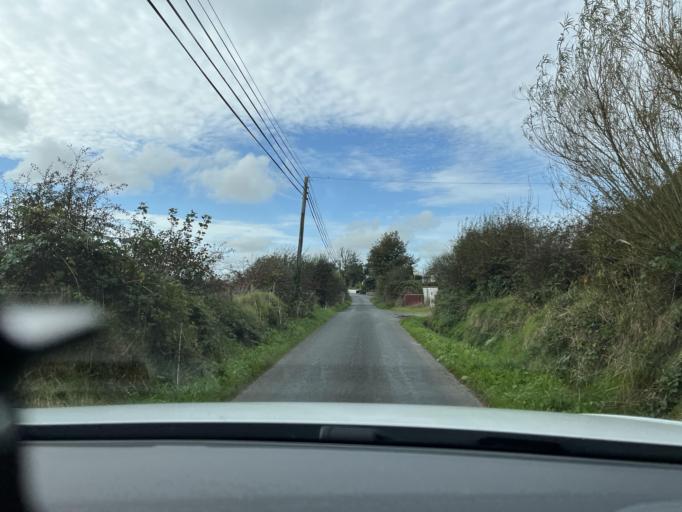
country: IE
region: Connaught
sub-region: Roscommon
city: Boyle
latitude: 54.0215
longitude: -8.3850
